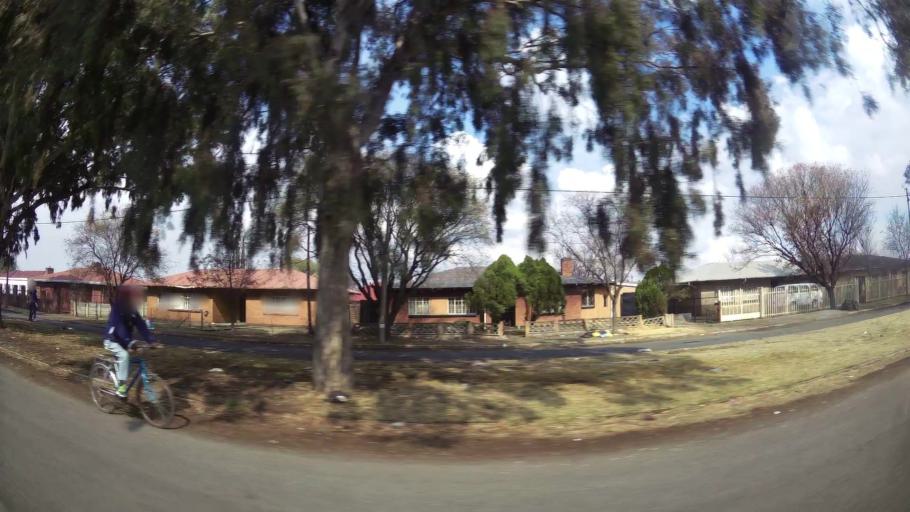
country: ZA
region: Gauteng
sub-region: Sedibeng District Municipality
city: Vereeniging
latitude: -26.6834
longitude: 27.9237
